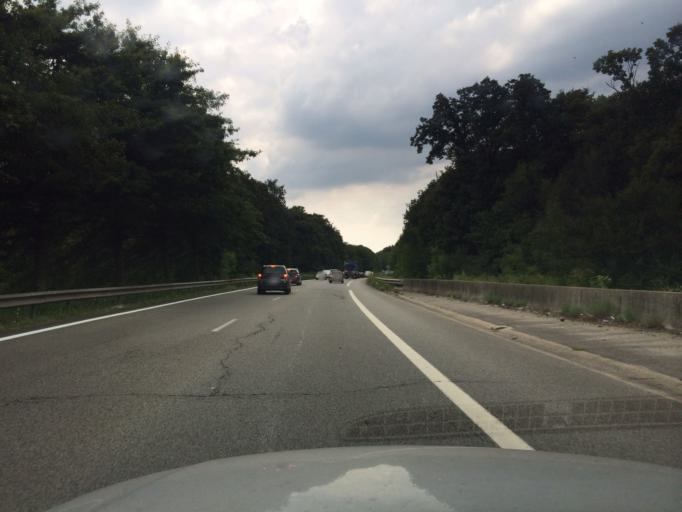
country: FR
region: Ile-de-France
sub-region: Departement des Yvelines
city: Rocquencourt
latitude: 48.8424
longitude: 2.0946
